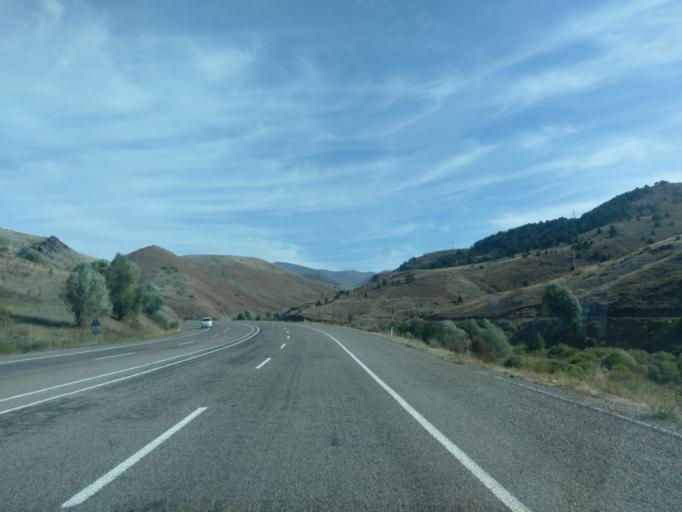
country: TR
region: Sivas
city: Imranli
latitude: 39.8480
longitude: 38.2931
